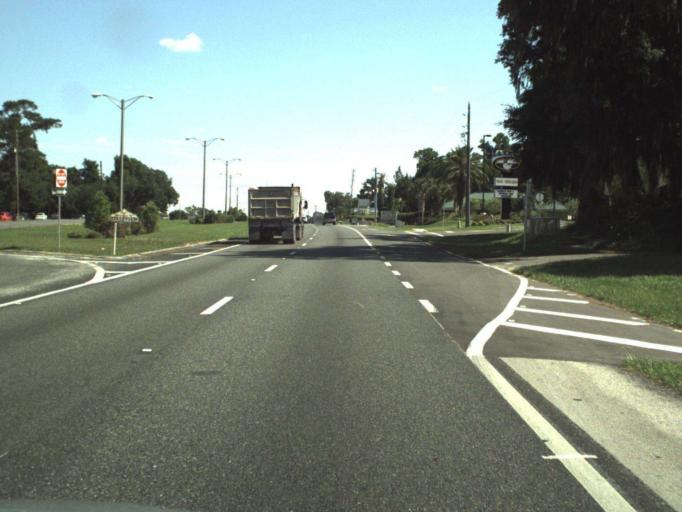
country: US
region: Florida
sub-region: Marion County
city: Belleview
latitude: 29.0702
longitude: -82.0711
